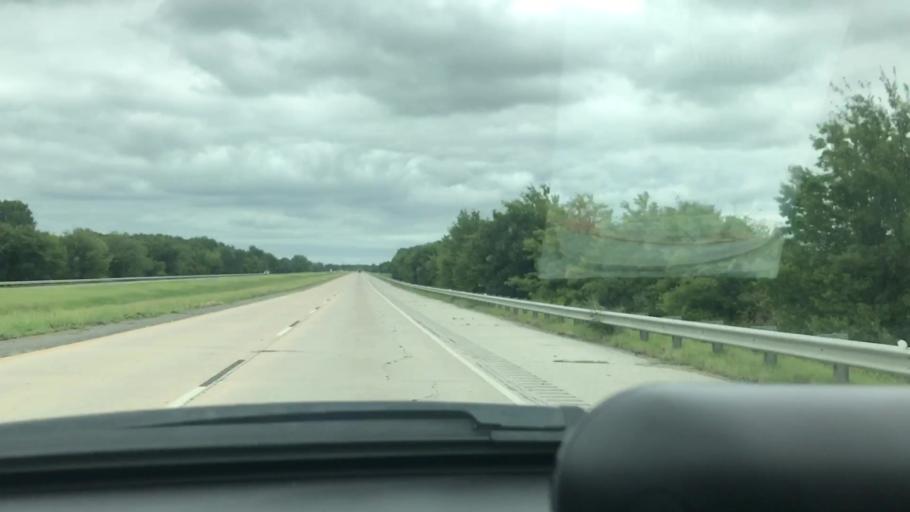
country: US
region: Oklahoma
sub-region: Wagoner County
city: Wagoner
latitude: 35.8914
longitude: -95.4026
